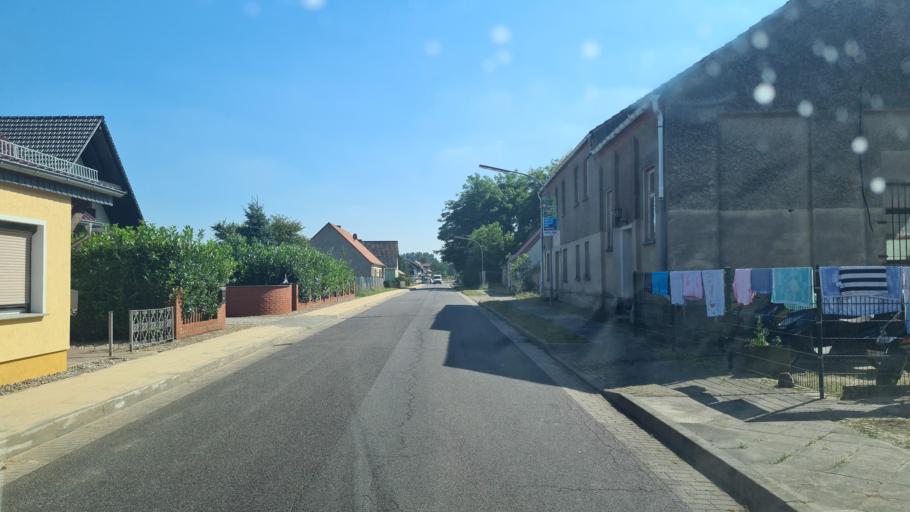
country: DE
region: Brandenburg
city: Friesack
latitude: 52.7286
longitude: 12.6259
